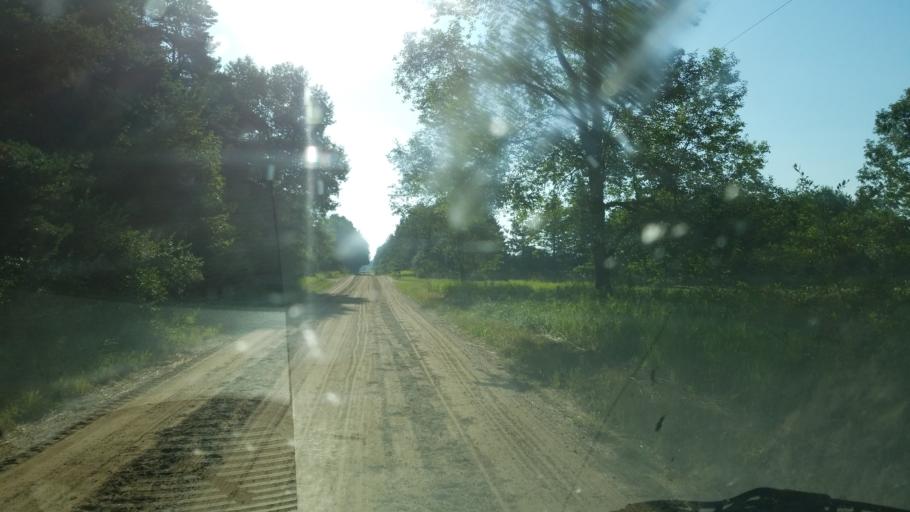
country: US
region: Michigan
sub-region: Mecosta County
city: Canadian Lakes
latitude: 43.5693
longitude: -85.4094
